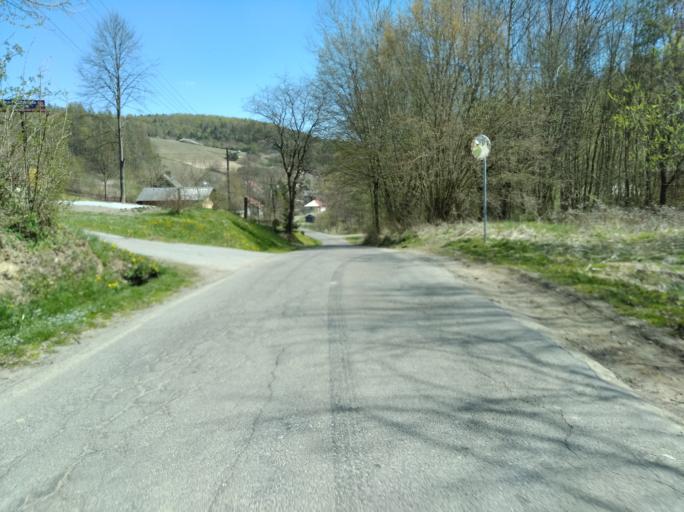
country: PL
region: Subcarpathian Voivodeship
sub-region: Powiat brzozowski
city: Dydnia
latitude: 49.7139
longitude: 22.1790
